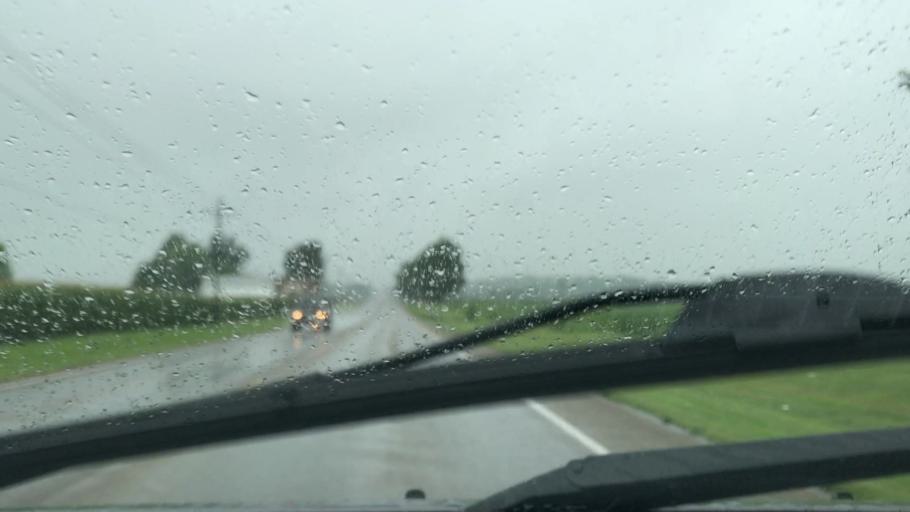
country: US
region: Indiana
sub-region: Hamilton County
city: Sheridan
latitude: 40.1184
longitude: -86.1830
